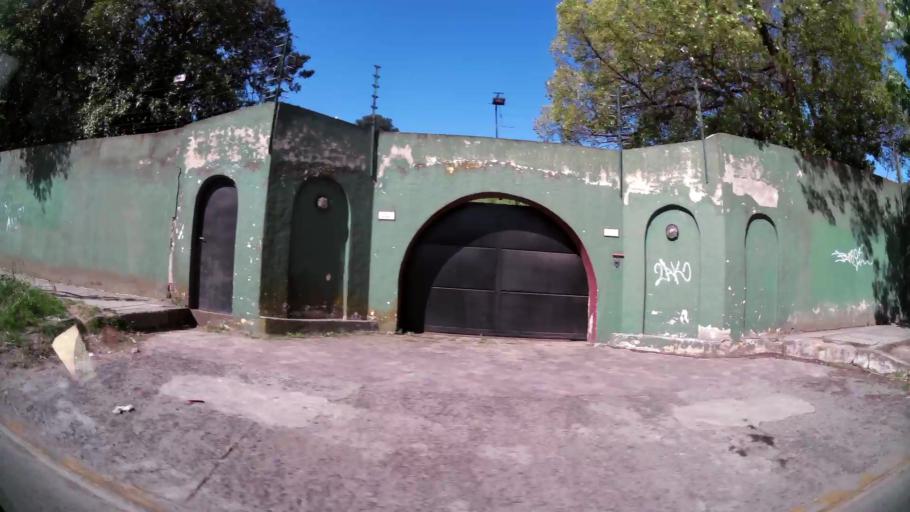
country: AR
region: Buenos Aires
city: Santa Catalina - Dique Lujan
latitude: -34.4751
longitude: -58.7051
